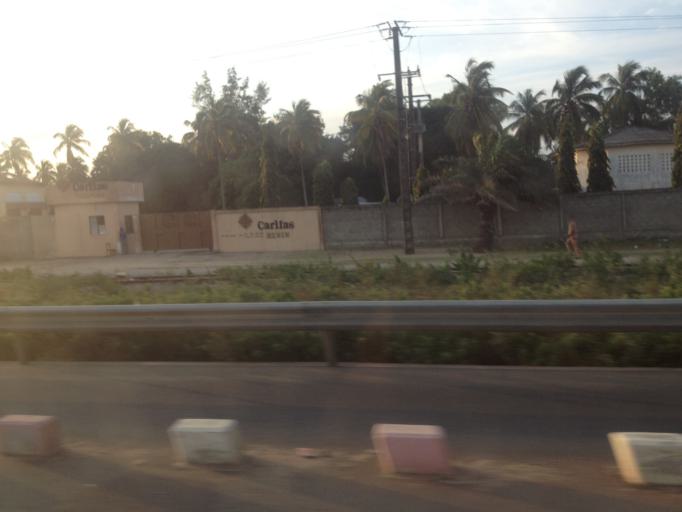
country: BJ
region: Queme
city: Porto-Novo
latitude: 6.3762
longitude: 2.5780
